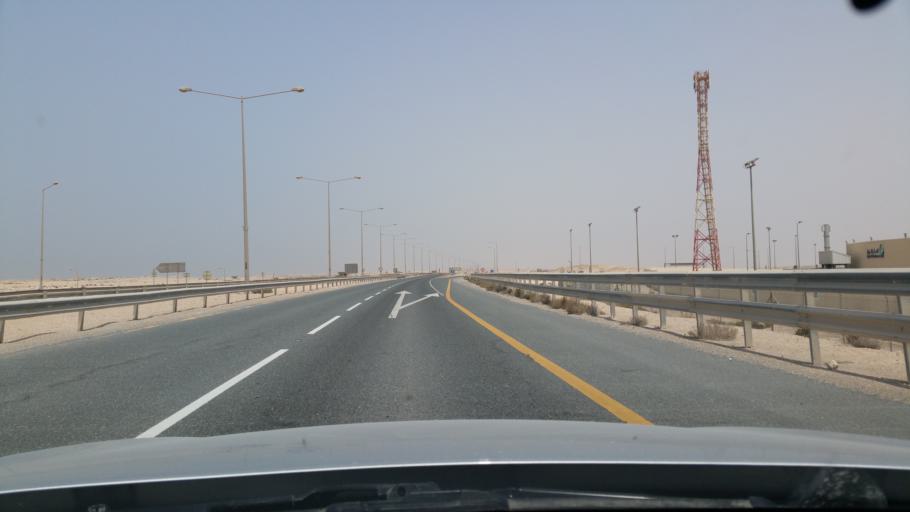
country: QA
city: Umm Bab
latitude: 25.2319
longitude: 50.8020
